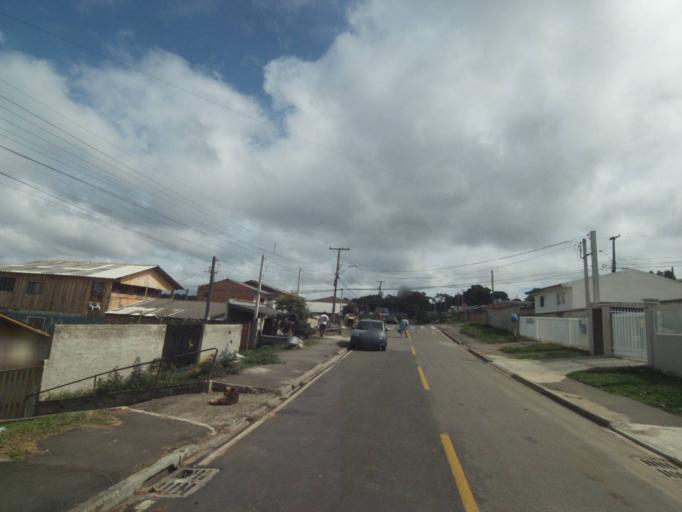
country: BR
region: Parana
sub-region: Quatro Barras
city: Quatro Barras
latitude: -25.3432
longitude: -49.0887
